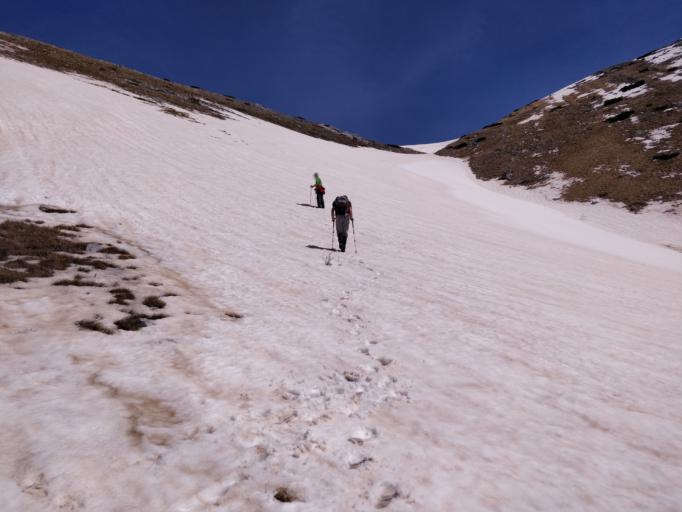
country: HR
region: Zadarska
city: Starigrad
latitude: 44.3309
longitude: 15.5632
